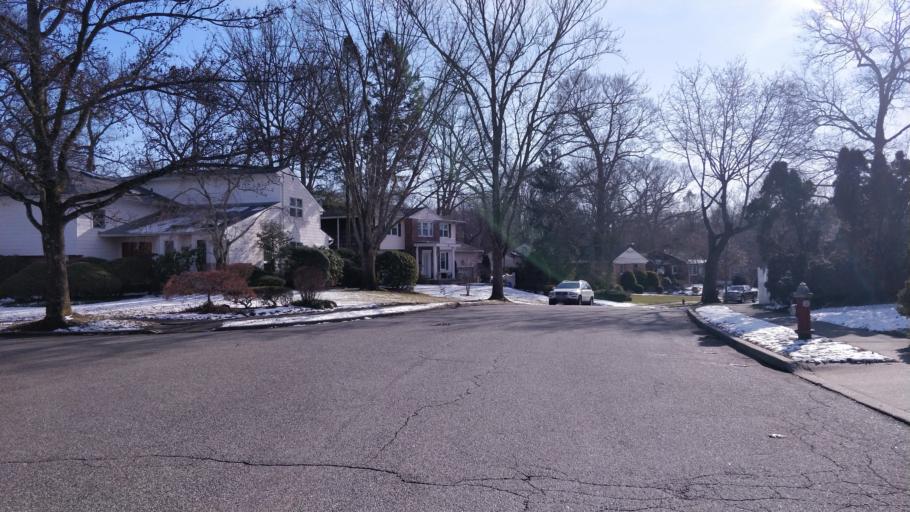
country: US
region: New York
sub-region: Nassau County
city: East Norwich
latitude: 40.8545
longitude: -73.5258
